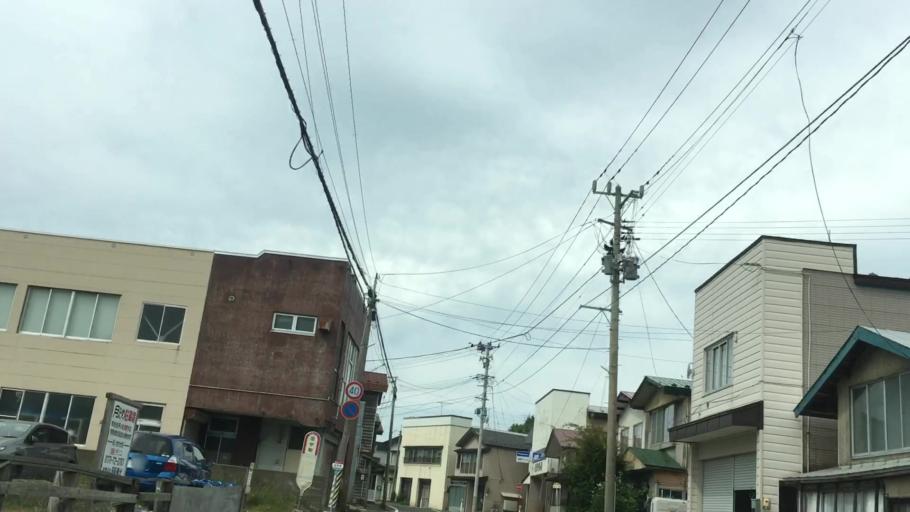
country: JP
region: Aomori
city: Shimokizukuri
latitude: 40.7780
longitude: 140.2172
